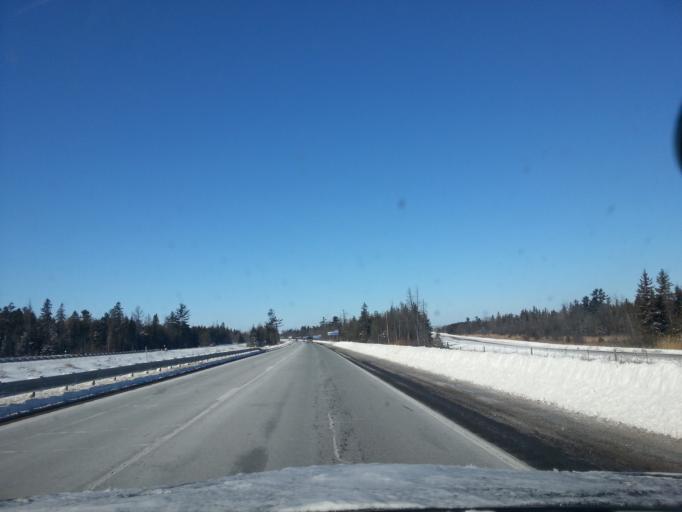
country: CA
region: Ontario
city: Arnprior
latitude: 45.3495
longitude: -76.2060
